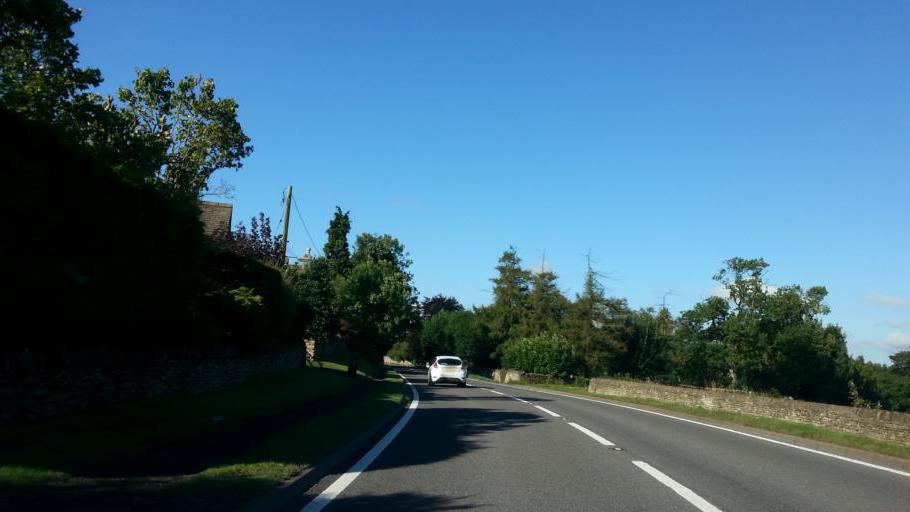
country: GB
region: England
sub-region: District of Rutland
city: Ketton
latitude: 52.6156
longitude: -0.5268
